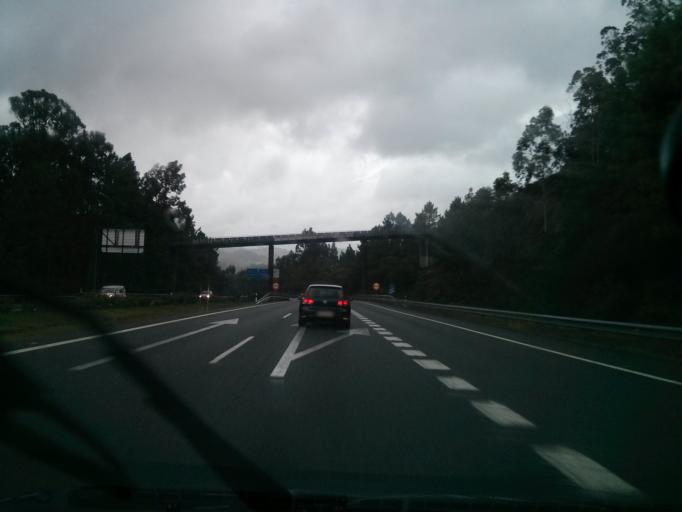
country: ES
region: Galicia
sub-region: Provincia de Pontevedra
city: Porrino
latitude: 42.1666
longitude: -8.6143
